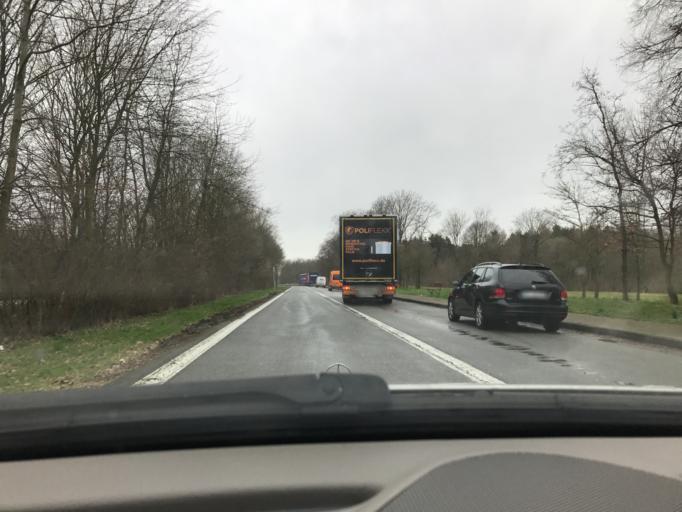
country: DE
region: North Rhine-Westphalia
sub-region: Regierungsbezirk Detmold
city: Wunnenberg
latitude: 51.5890
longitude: 8.6487
